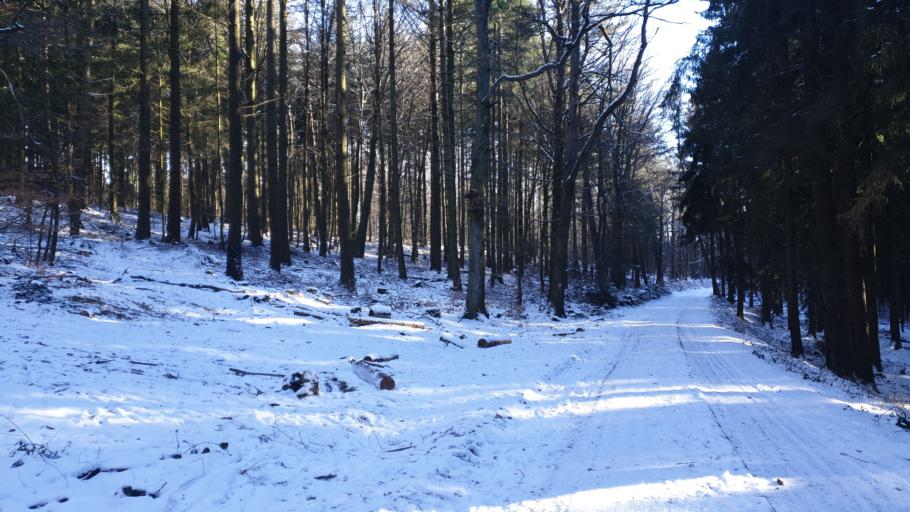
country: DE
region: Hesse
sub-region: Regierungsbezirk Darmstadt
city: Beerfelden
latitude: 49.5449
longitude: 8.9919
